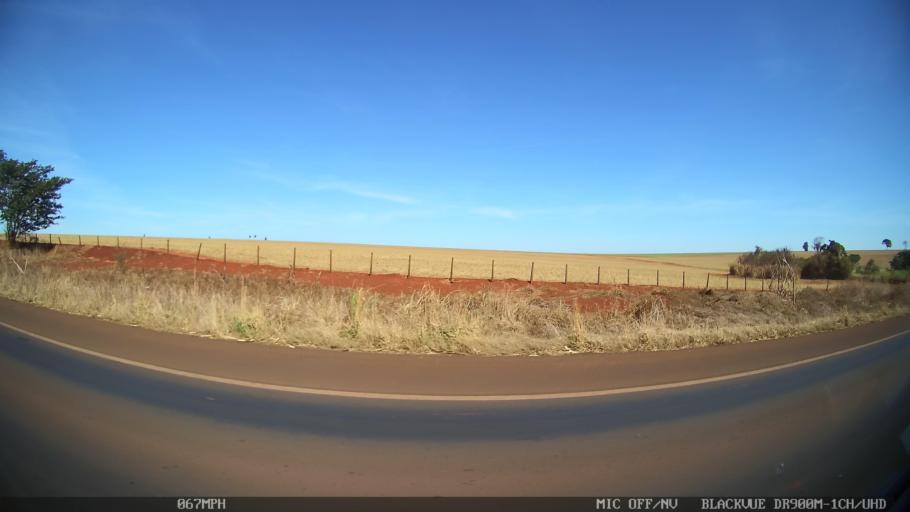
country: BR
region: Sao Paulo
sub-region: Sao Joaquim Da Barra
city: Sao Joaquim da Barra
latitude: -20.5099
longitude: -47.9118
